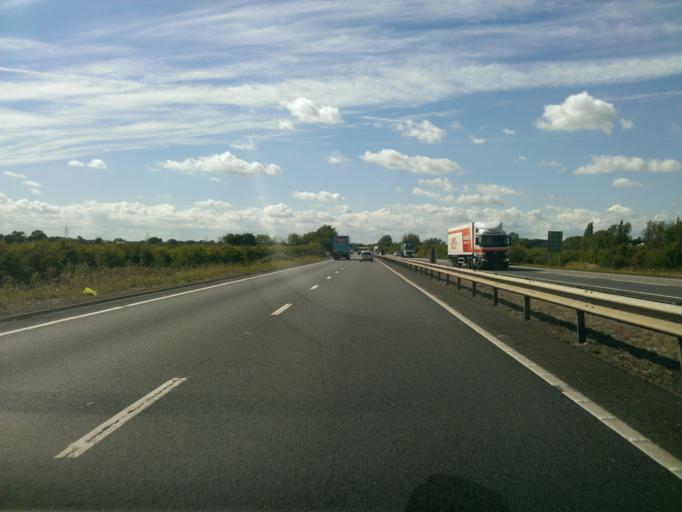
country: GB
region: England
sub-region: Bedford
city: Swineshead
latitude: 52.3641
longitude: -0.4321
